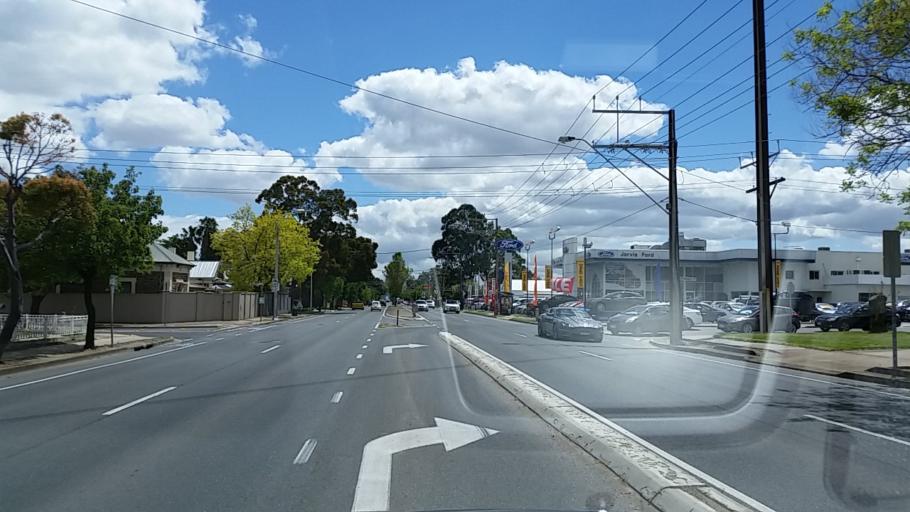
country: AU
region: South Australia
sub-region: Norwood Payneham St Peters
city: Trinity Gardens
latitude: -34.9127
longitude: 138.6404
